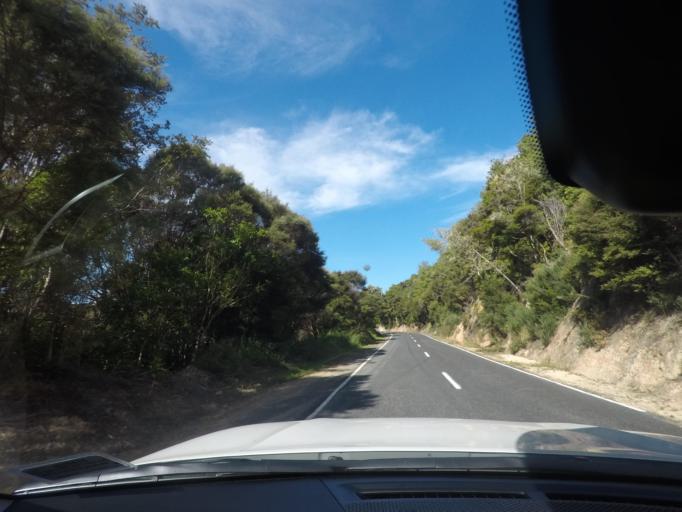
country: NZ
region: Northland
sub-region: Whangarei
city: Ngunguru
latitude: -35.6646
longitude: 174.4793
